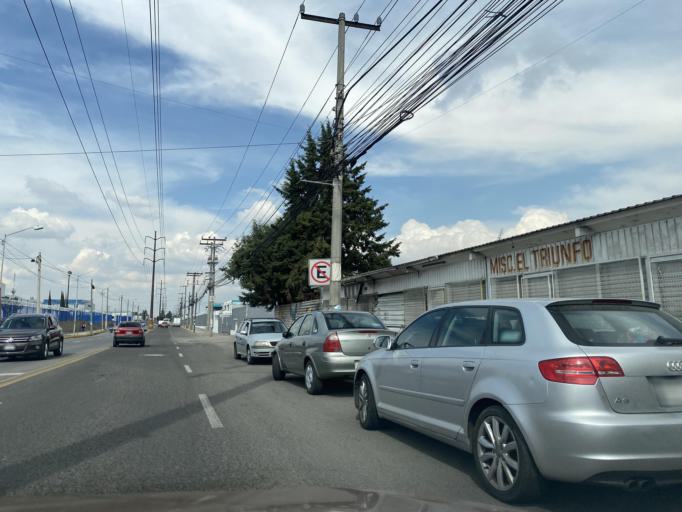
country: IN
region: Karnataka
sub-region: Dakshina Kannada
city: Puttur
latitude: 12.7363
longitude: 75.1856
